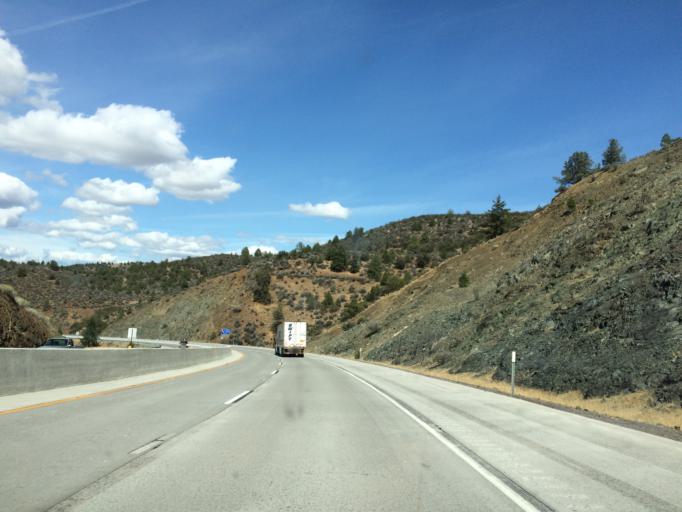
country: US
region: California
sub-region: Siskiyou County
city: Montague
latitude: 41.8447
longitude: -122.5710
